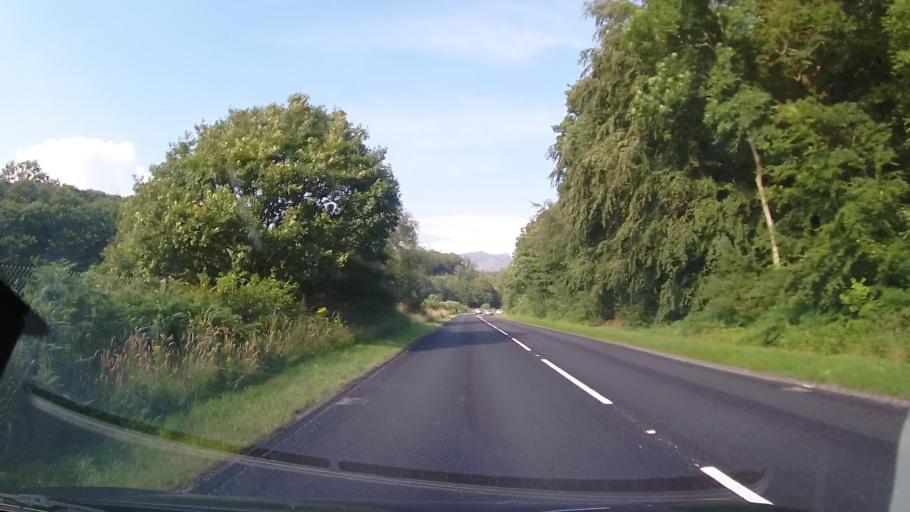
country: GB
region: Wales
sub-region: Gwynedd
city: Penrhyndeudraeth
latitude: 52.9377
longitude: -4.0518
